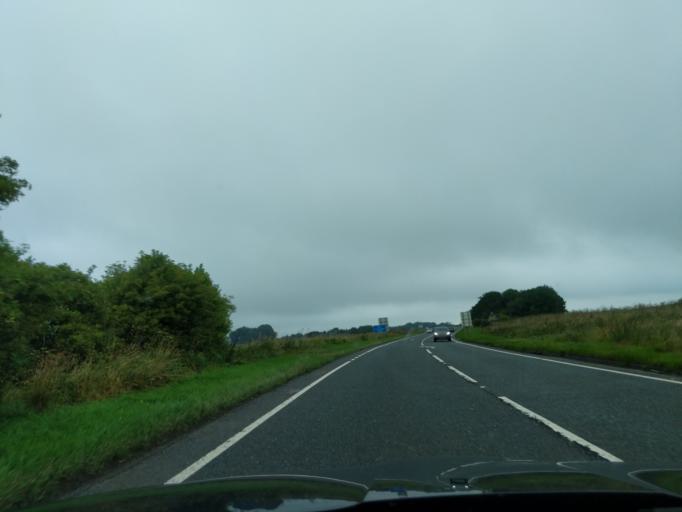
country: GB
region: England
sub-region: Northumberland
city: Ellingham
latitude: 55.4940
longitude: -1.7327
